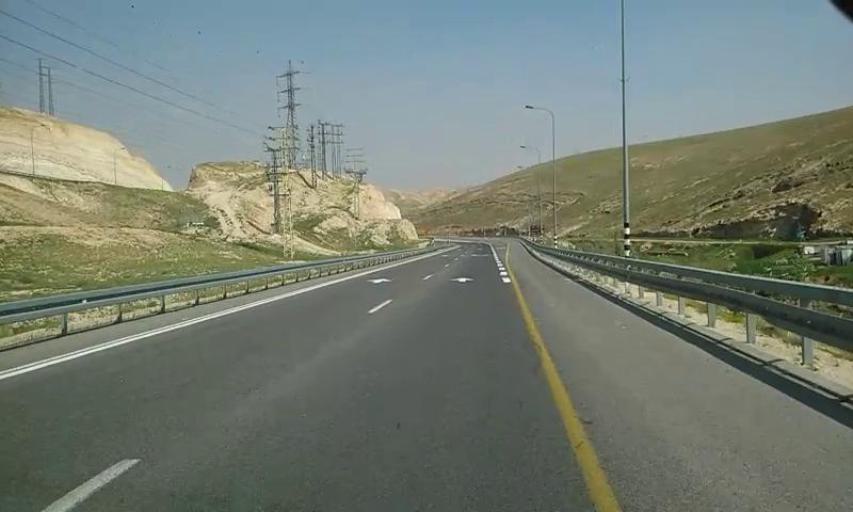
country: PS
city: Az Za`ayyim
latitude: 31.8087
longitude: 35.3361
